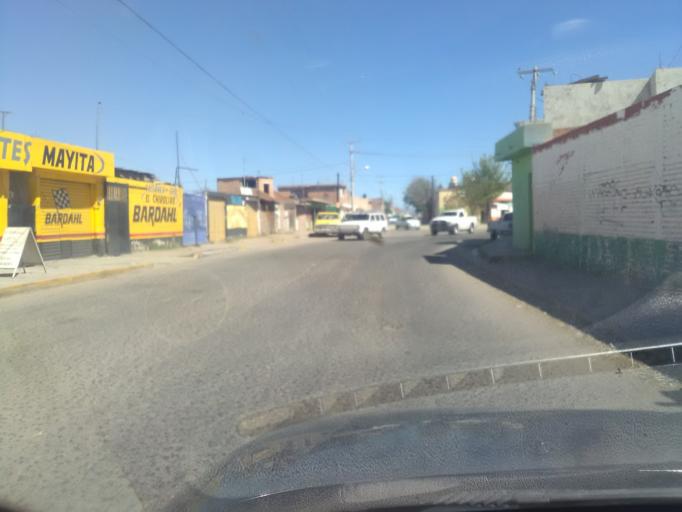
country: MX
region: Durango
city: Victoria de Durango
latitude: 24.0106
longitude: -104.6498
